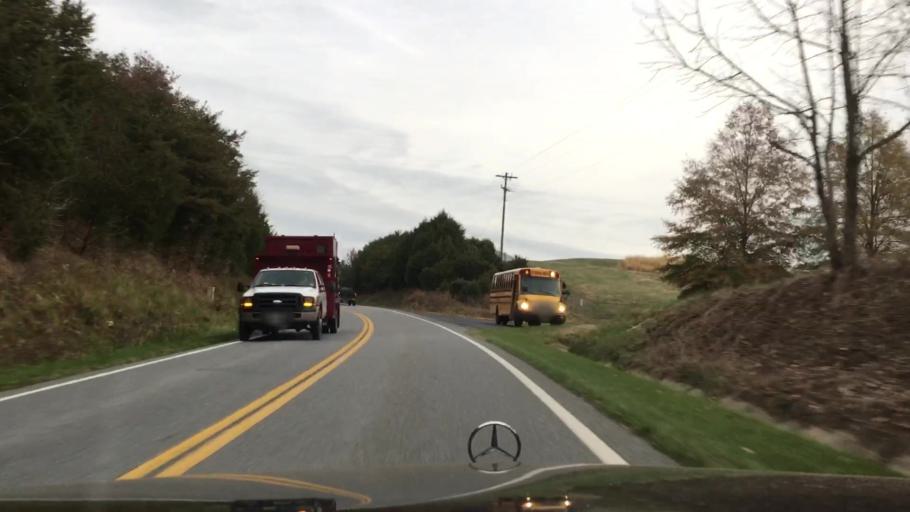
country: US
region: Virginia
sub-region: Campbell County
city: Altavista
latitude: 37.2113
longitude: -79.2999
